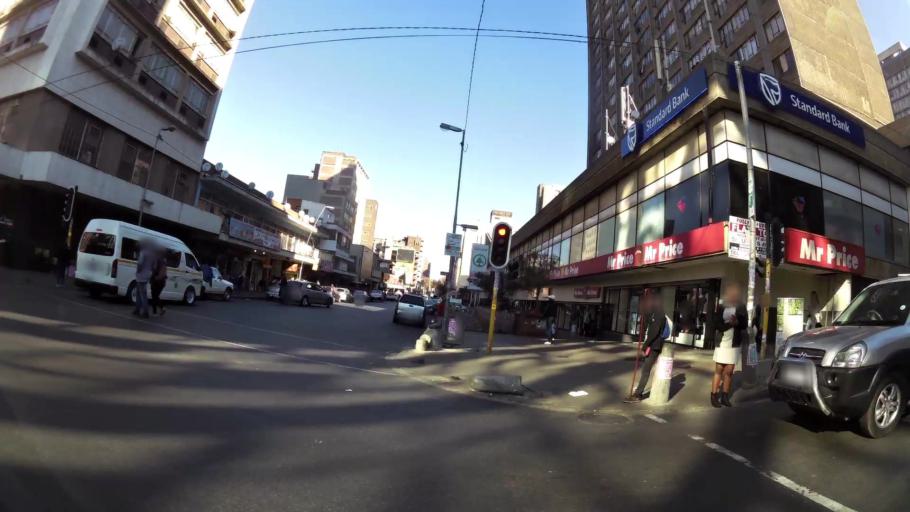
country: ZA
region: Gauteng
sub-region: City of Johannesburg Metropolitan Municipality
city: Johannesburg
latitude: -26.1896
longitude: 28.0491
